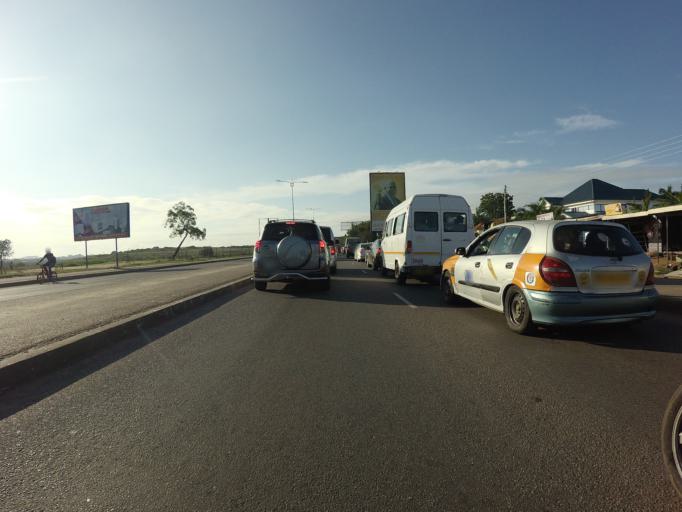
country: GH
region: Greater Accra
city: Accra
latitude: 5.5516
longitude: -0.2304
